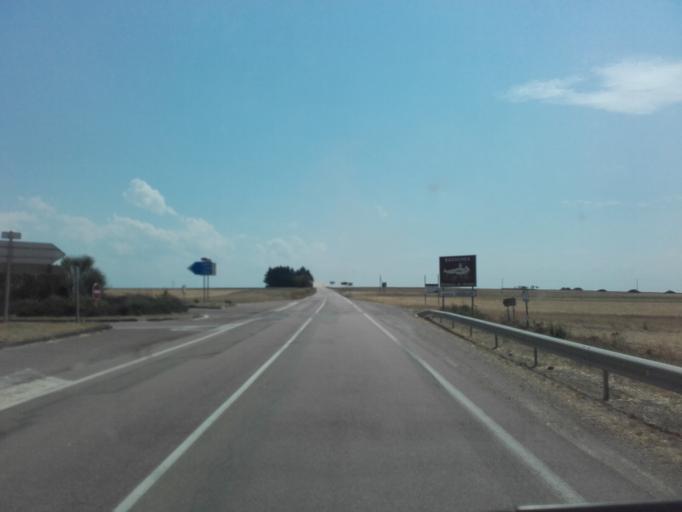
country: FR
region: Bourgogne
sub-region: Departement de l'Yonne
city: Joux-la-Ville
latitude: 47.6596
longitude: 3.8770
